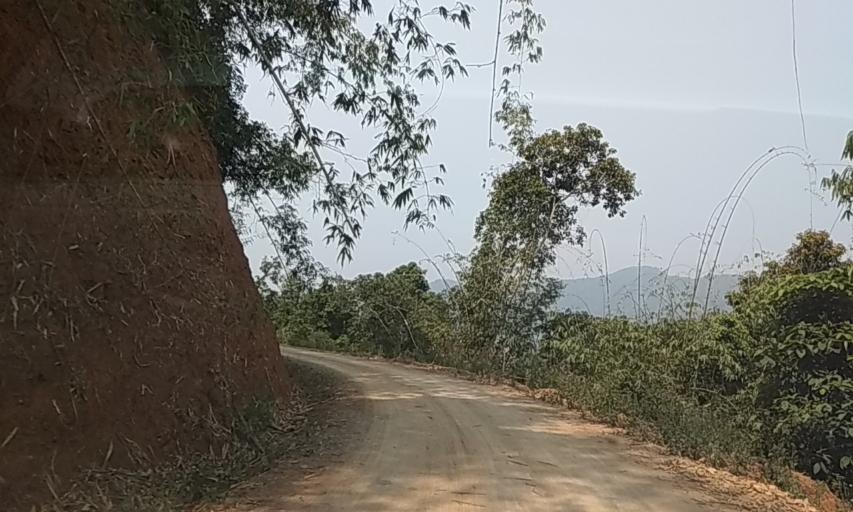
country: LA
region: Phongsali
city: Phongsali
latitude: 21.4643
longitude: 102.4198
